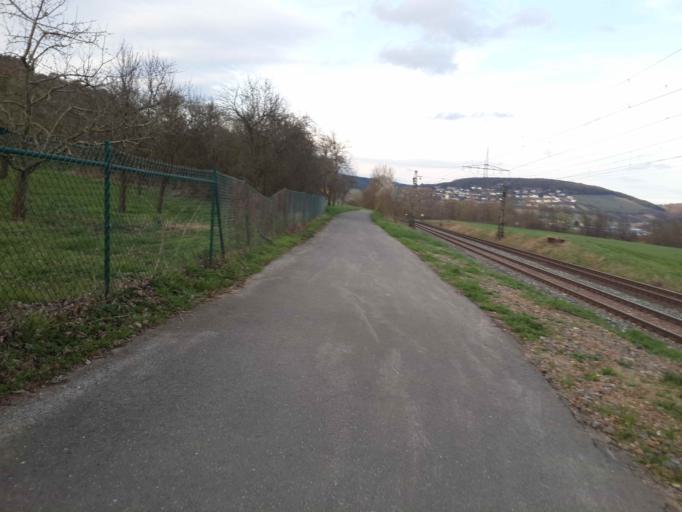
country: DE
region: Baden-Wuerttemberg
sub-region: Regierungsbezirk Stuttgart
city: Lauda-Konigshofen
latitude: 49.5351
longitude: 9.7170
